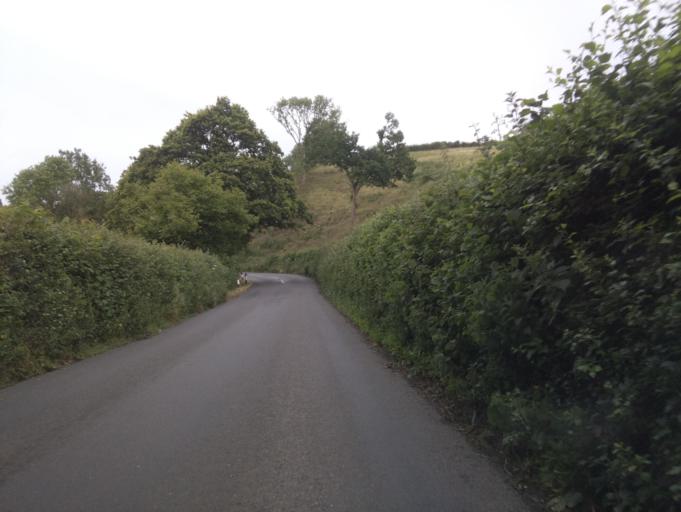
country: GB
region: England
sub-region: Devon
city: Chudleigh
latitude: 50.6263
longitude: -3.6403
